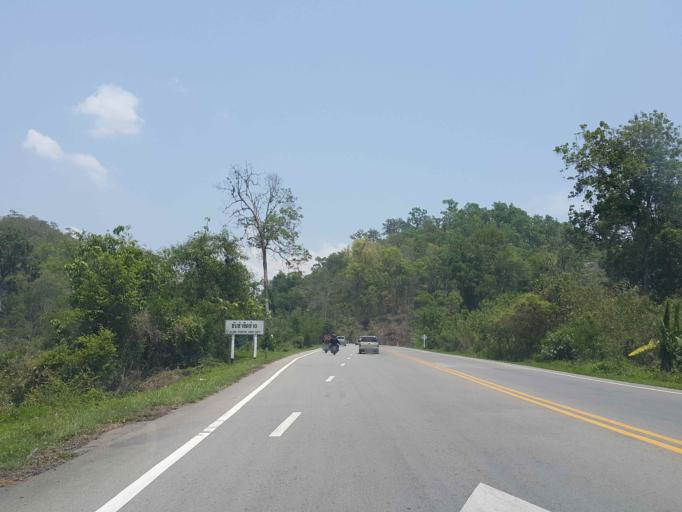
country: TH
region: Chiang Mai
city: Mae On
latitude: 18.9438
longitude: 99.2348
